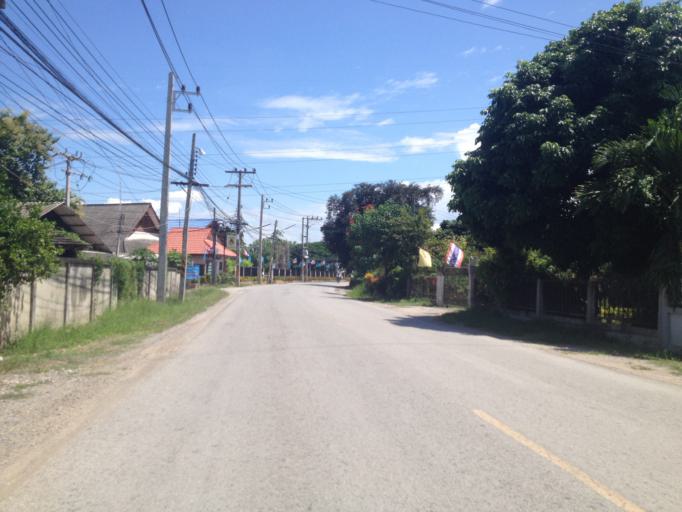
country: TH
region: Chiang Mai
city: San Pa Tong
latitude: 18.6447
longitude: 98.9268
